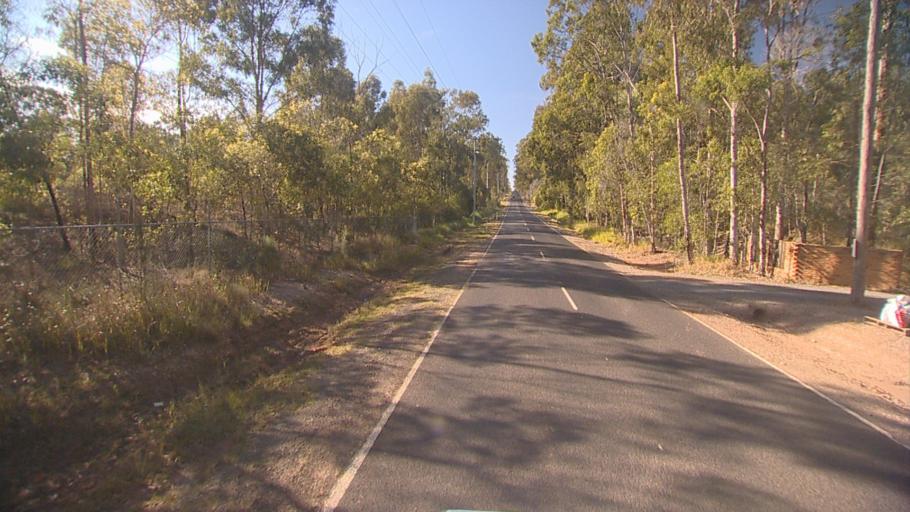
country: AU
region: Queensland
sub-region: Ipswich
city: Springfield Lakes
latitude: -27.6975
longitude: 152.9591
